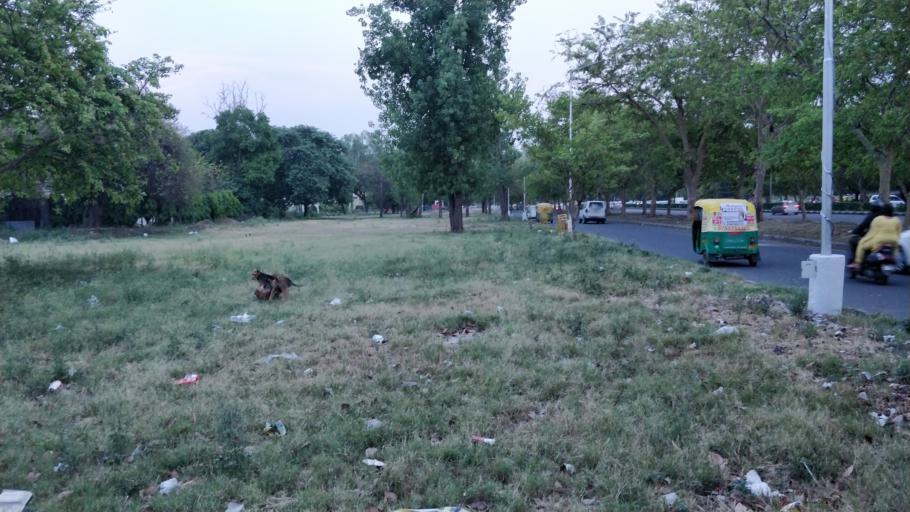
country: IN
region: Chandigarh
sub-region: Chandigarh
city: Chandigarh
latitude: 30.7228
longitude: 76.7718
